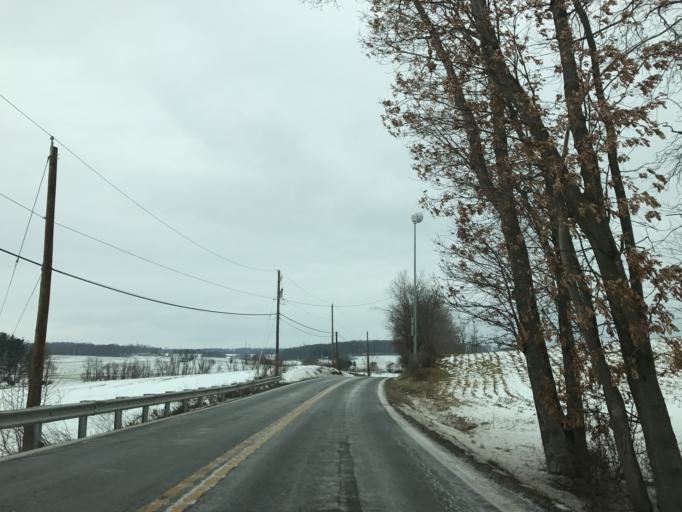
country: US
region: Pennsylvania
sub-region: York County
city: Susquehanna Trails
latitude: 39.6778
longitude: -76.4100
